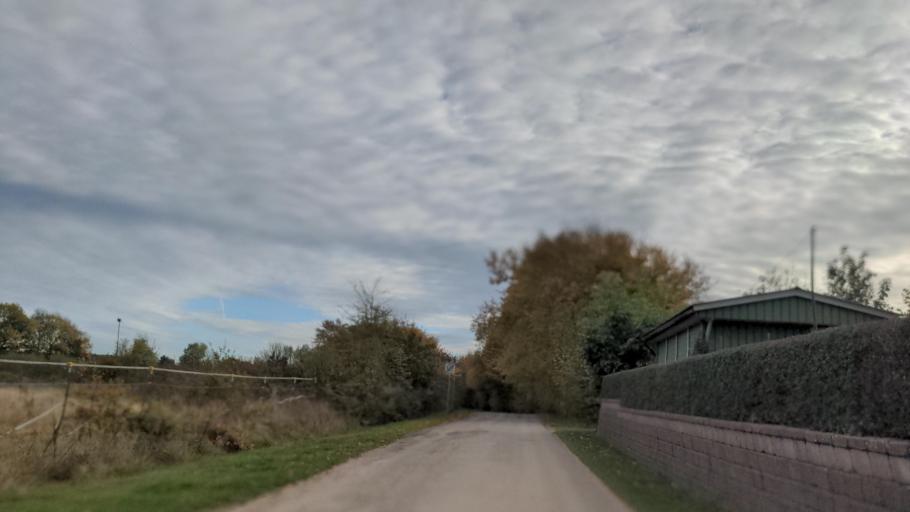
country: DE
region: Schleswig-Holstein
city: Bosdorf
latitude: 54.1280
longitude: 10.4997
